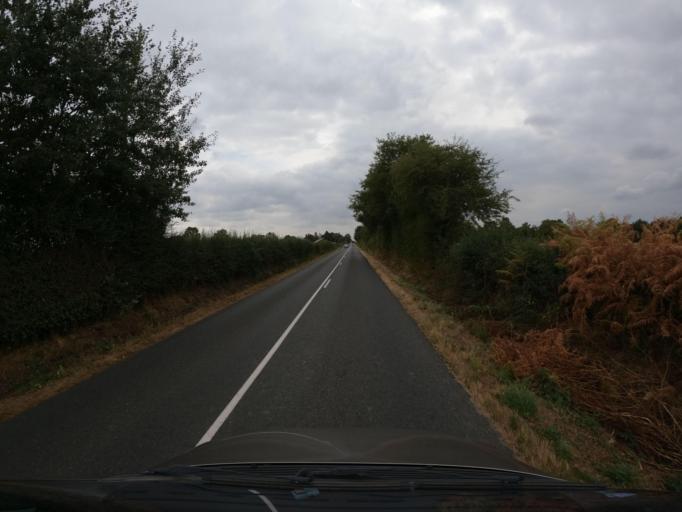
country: FR
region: Pays de la Loire
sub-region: Departement de Maine-et-Loire
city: La Romagne
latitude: 47.0412
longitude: -1.0361
